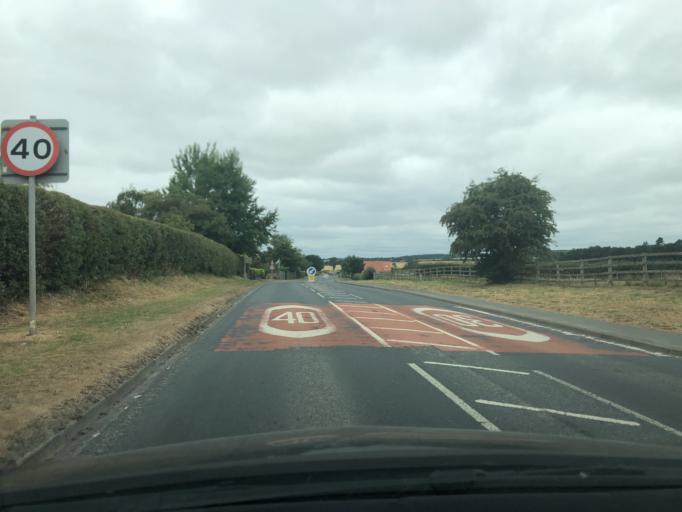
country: GB
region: England
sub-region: North Yorkshire
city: East Ayton
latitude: 54.2436
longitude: -0.4483
